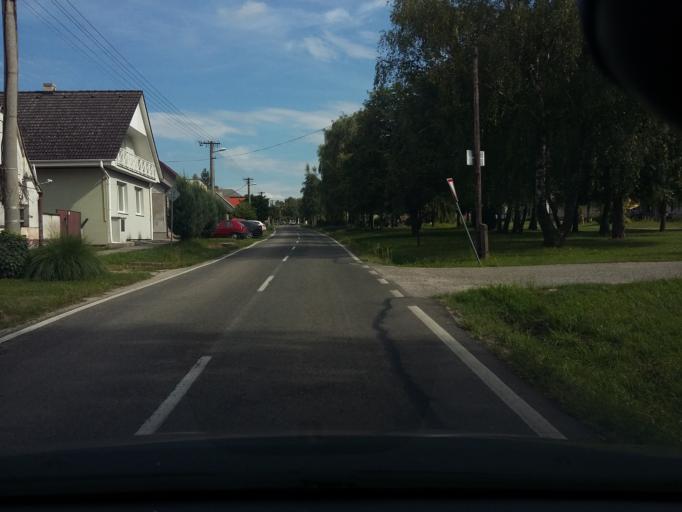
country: SK
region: Trnavsky
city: Gbely
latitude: 48.5804
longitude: 17.1814
